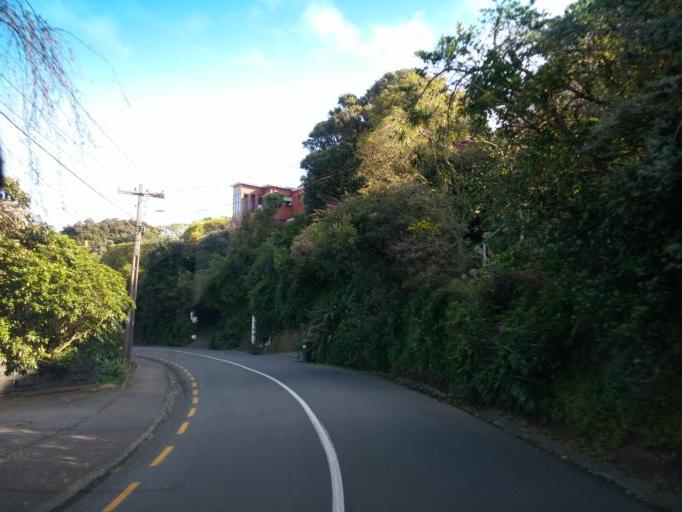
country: NZ
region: Wellington
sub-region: Wellington City
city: Wellington
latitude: -41.3231
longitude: 174.8236
